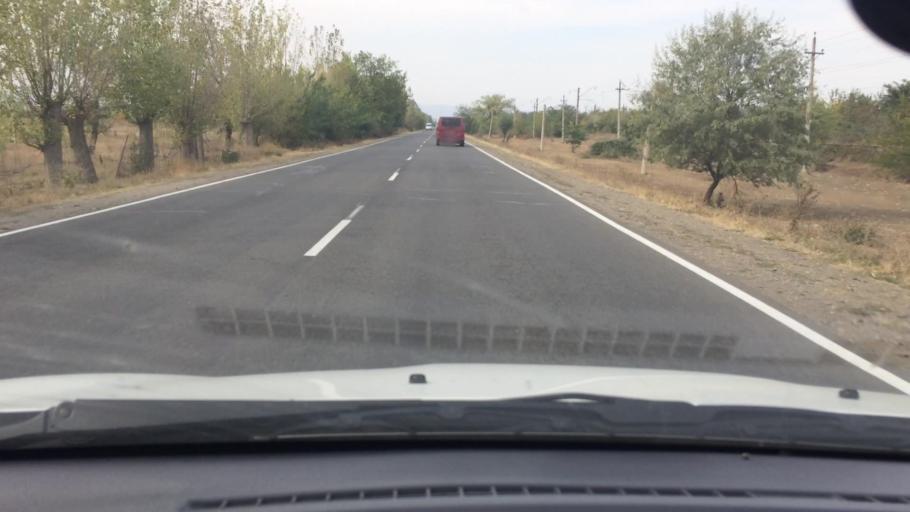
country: GE
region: Kvemo Kartli
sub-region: Marneuli
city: Marneuli
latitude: 41.4435
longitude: 44.8164
